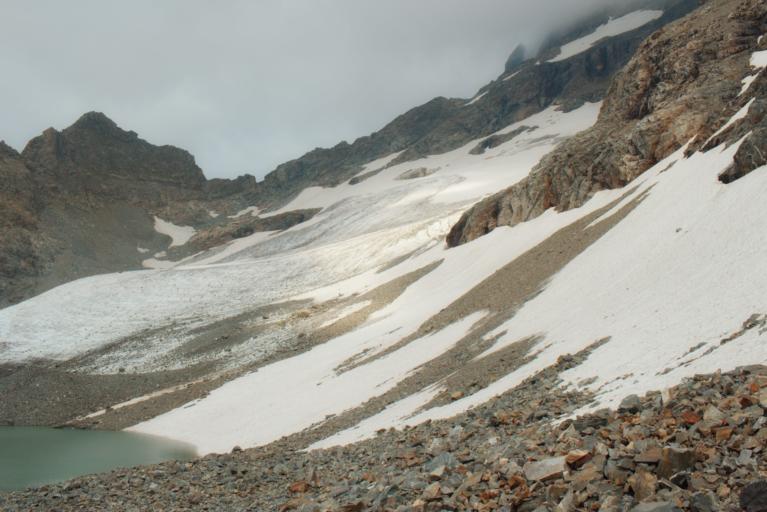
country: RU
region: Karachayevo-Cherkesiya
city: Nizhniy Arkhyz
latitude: 43.4255
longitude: 41.2528
